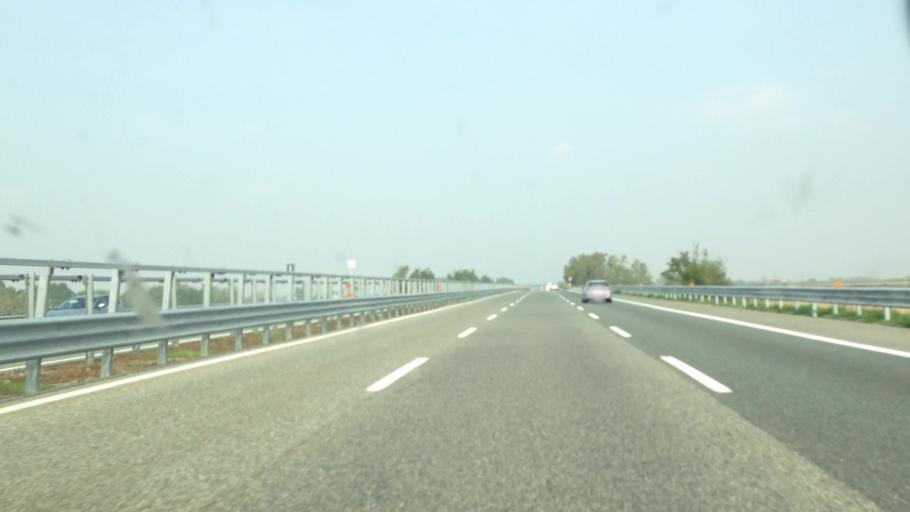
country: IT
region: Piedmont
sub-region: Provincia di Vercelli
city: Caresana
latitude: 45.2034
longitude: 8.4884
